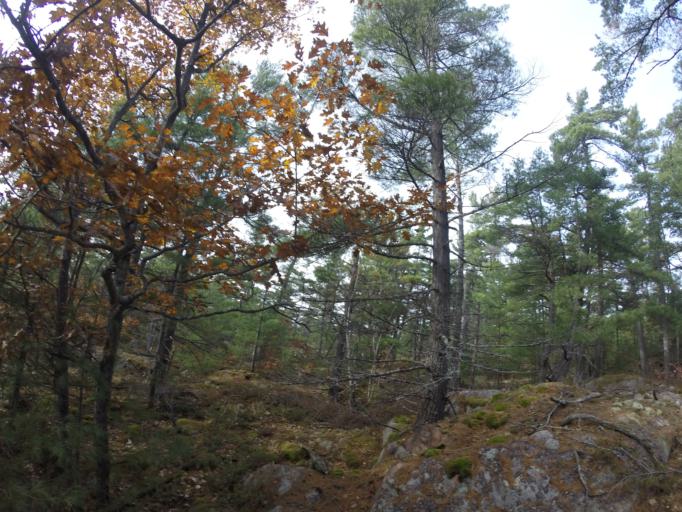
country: CA
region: Ontario
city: Espanola
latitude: 45.9694
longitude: -81.4861
